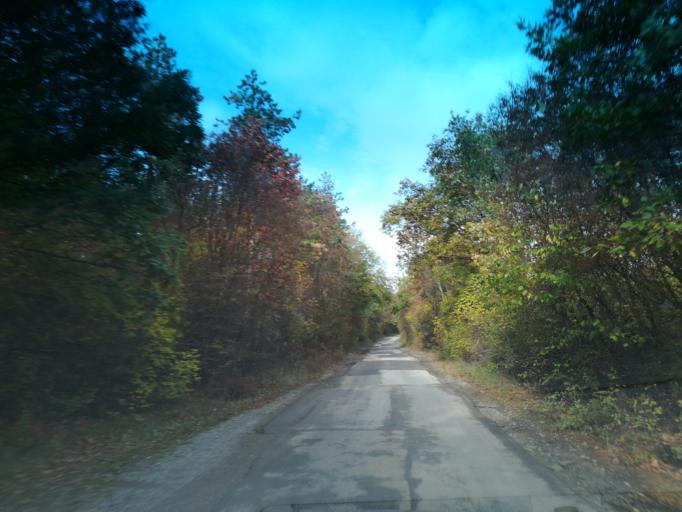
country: BG
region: Stara Zagora
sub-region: Obshtina Nikolaevo
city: Elkhovo
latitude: 42.3192
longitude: 25.4040
